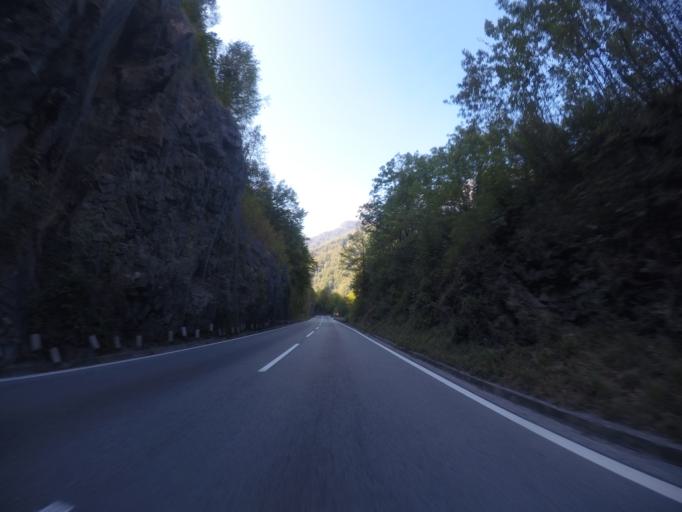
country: ME
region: Opstina Kolasin
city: Kolasin
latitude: 42.8128
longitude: 19.3949
